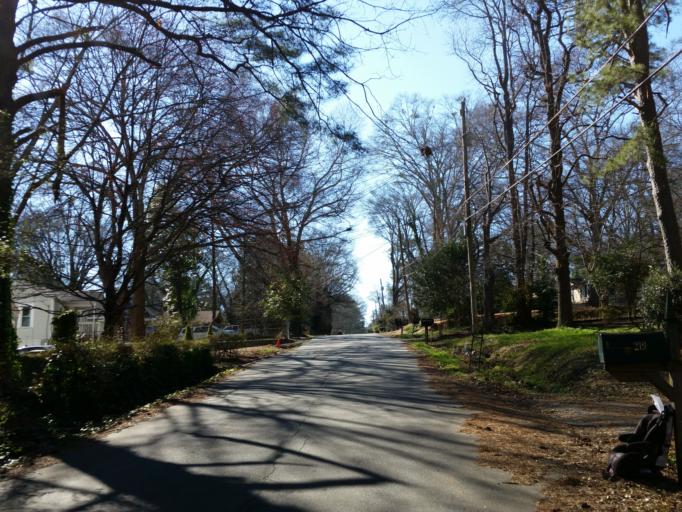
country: US
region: Georgia
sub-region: Cobb County
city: Marietta
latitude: 33.9374
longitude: -84.5466
